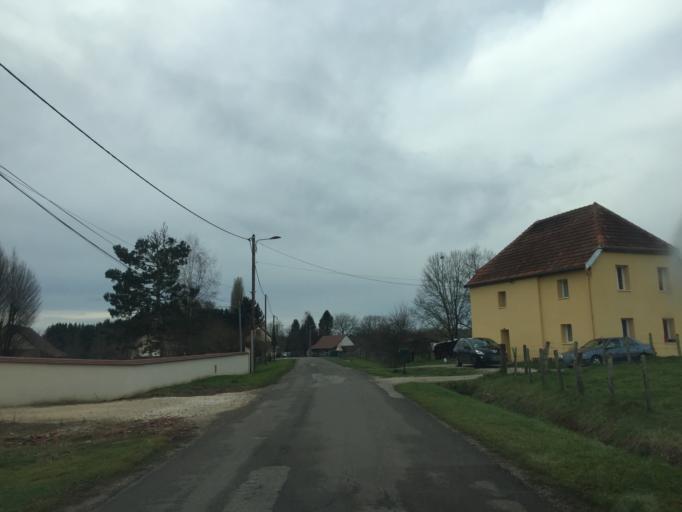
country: FR
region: Franche-Comte
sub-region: Departement du Jura
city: Chaussin
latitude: 46.9032
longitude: 5.4550
